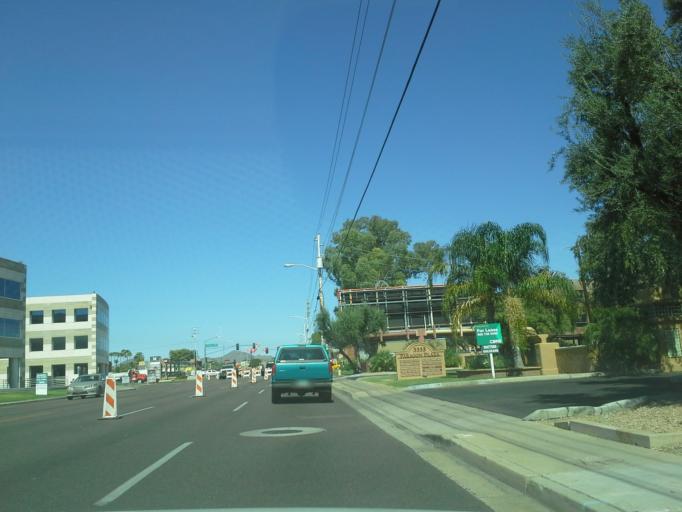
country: US
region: Arizona
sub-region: Maricopa County
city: Phoenix
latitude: 33.5151
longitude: -112.0649
